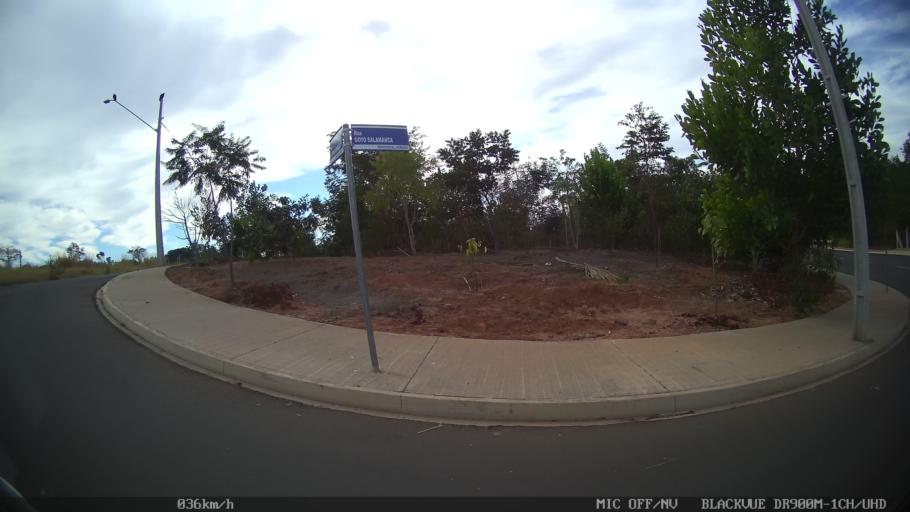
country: BR
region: Sao Paulo
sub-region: Catanduva
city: Catanduva
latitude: -21.1409
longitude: -49.0057
